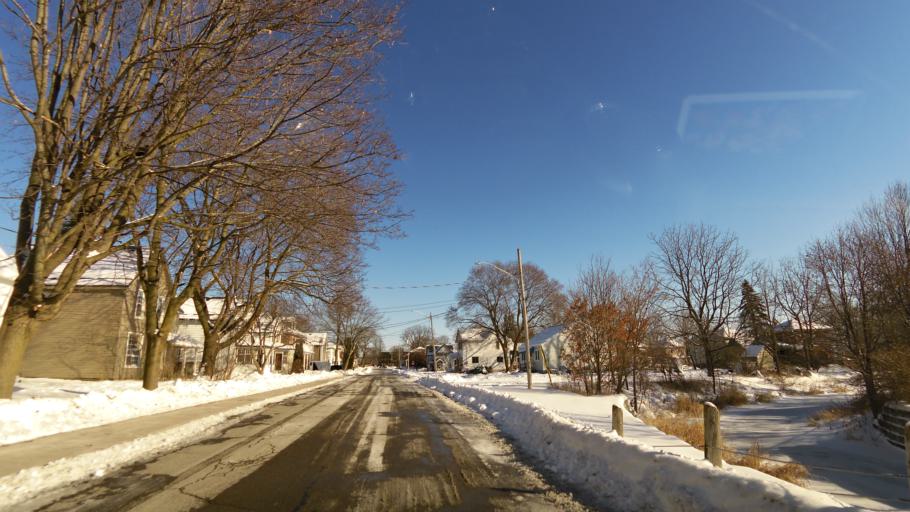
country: CA
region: Ontario
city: Quinte West
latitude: 44.3070
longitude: -77.8048
